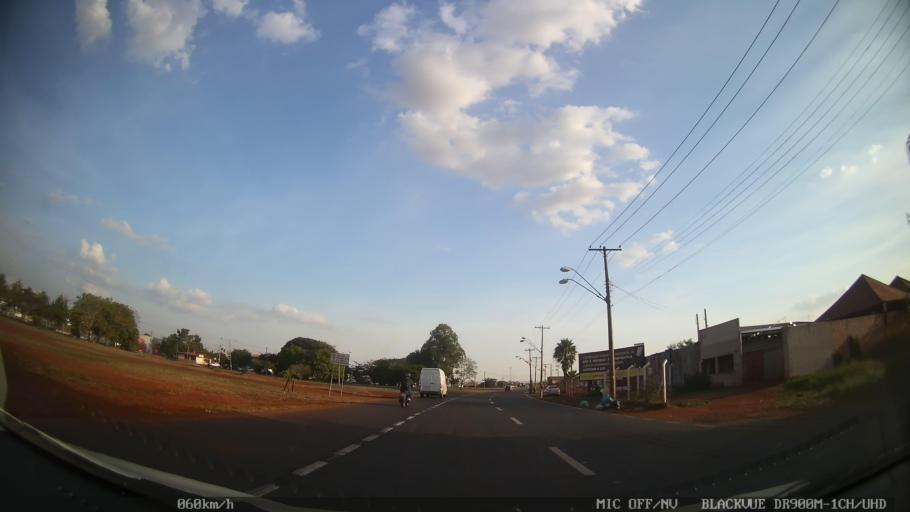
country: BR
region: Sao Paulo
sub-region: Ribeirao Preto
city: Ribeirao Preto
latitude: -21.1271
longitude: -47.7866
